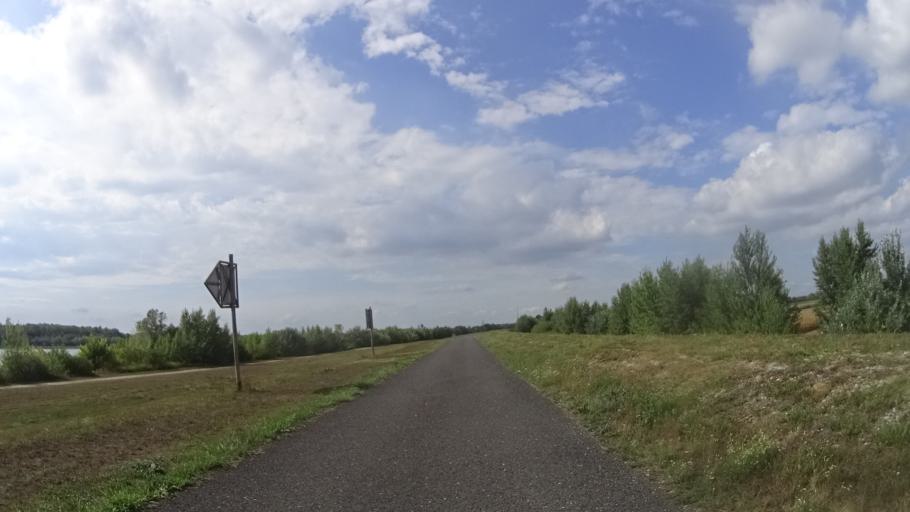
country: SK
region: Trnavsky
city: Gabcikovo
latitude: 47.8653
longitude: 17.5595
